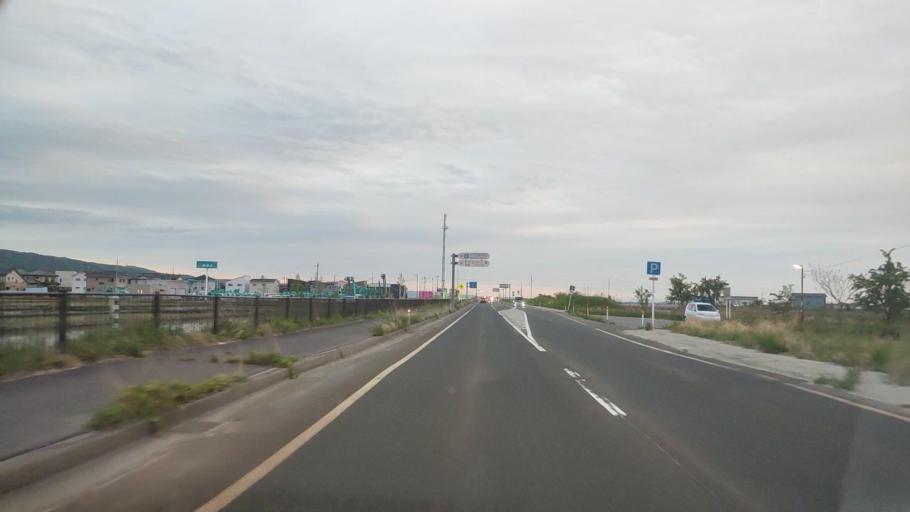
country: JP
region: Niigata
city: Niitsu-honcho
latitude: 37.7541
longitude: 139.0900
